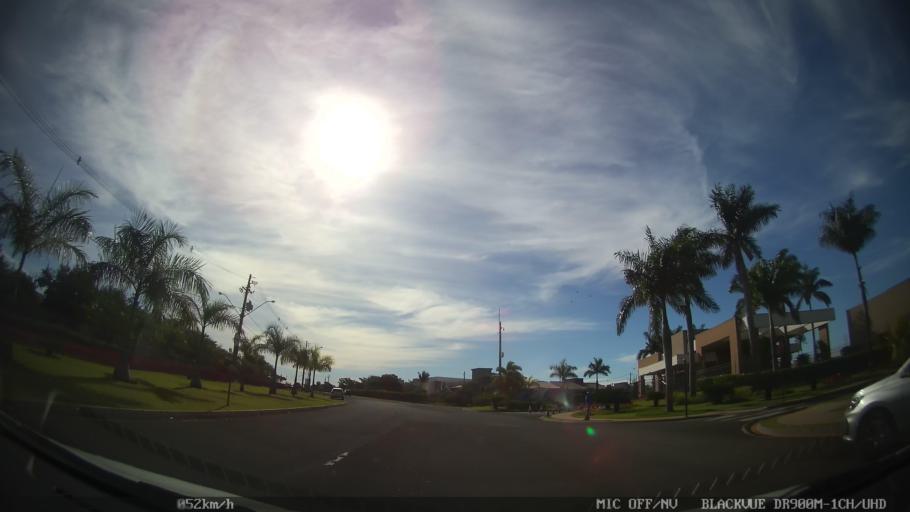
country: BR
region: Sao Paulo
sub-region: Sao Jose Do Rio Preto
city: Sao Jose do Rio Preto
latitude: -20.8091
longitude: -49.3295
